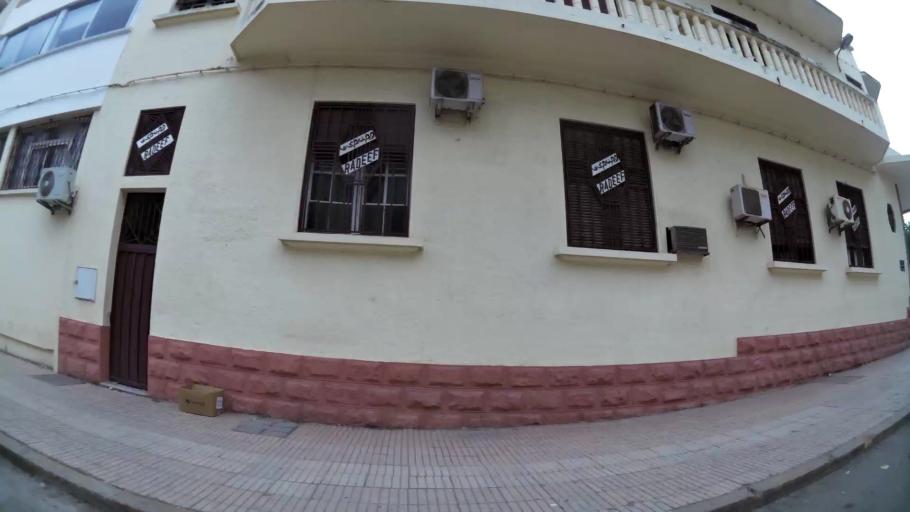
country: MA
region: Fes-Boulemane
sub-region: Fes
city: Fes
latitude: 34.0408
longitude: -5.0017
